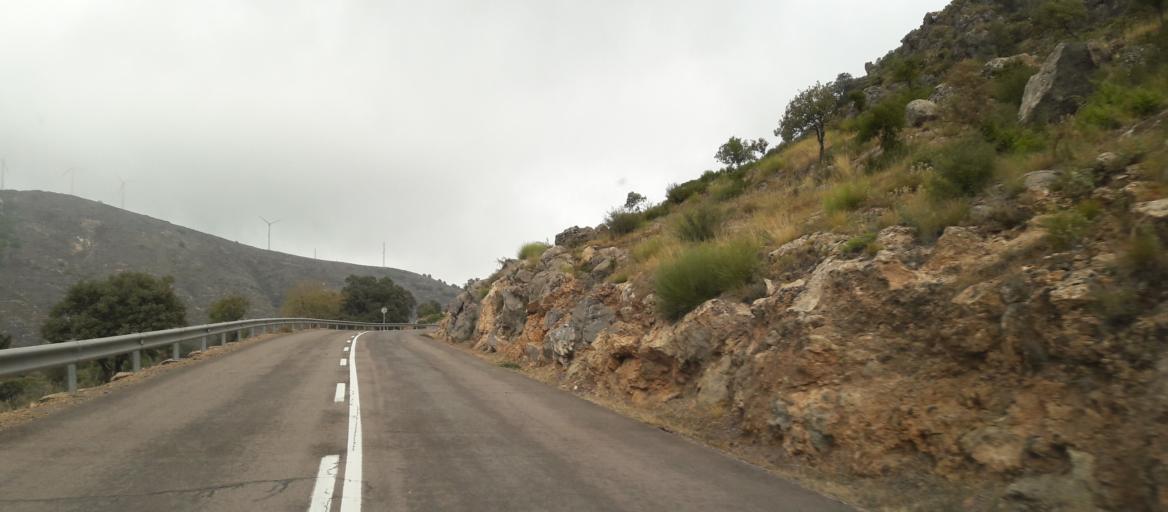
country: ES
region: Andalusia
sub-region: Provincia de Almeria
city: Enix
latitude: 36.8906
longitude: -2.6209
